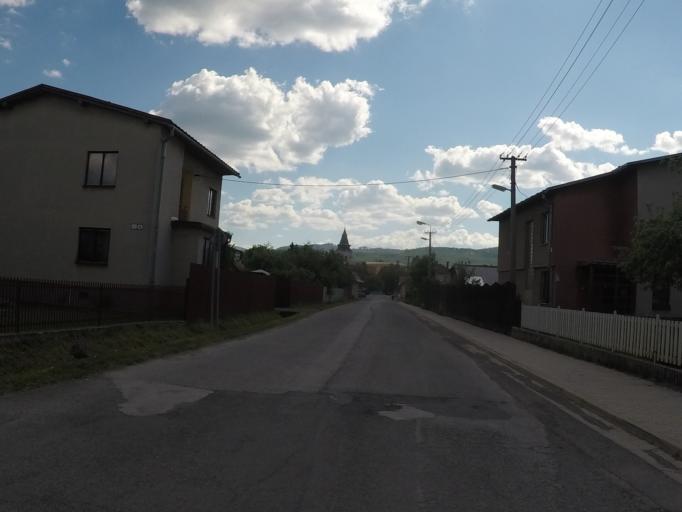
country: SK
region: Presovsky
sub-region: Okres Poprad
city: Poprad
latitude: 48.9972
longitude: 20.3607
